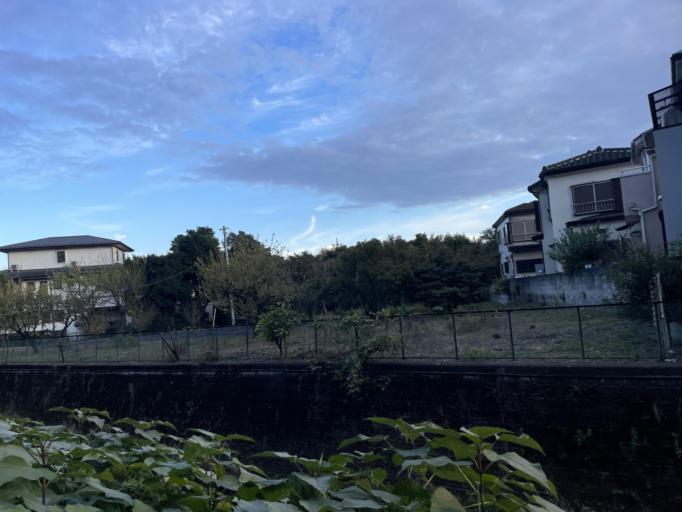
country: JP
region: Saitama
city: Wako
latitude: 35.7708
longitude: 139.6133
